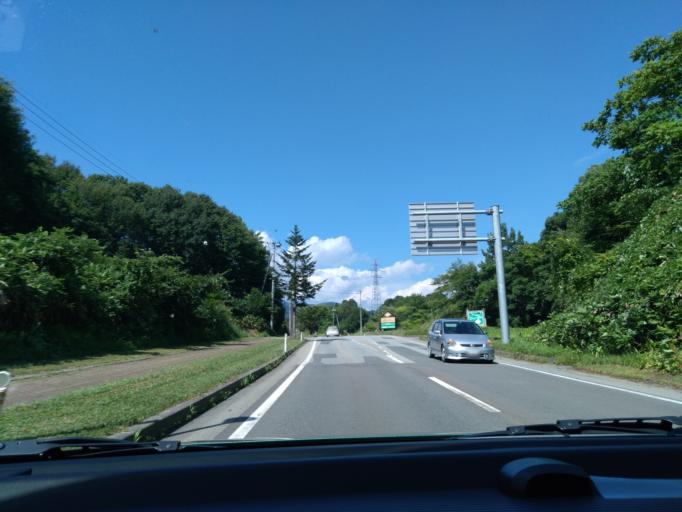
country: JP
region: Akita
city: Kakunodatemachi
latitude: 39.7412
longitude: 140.7188
